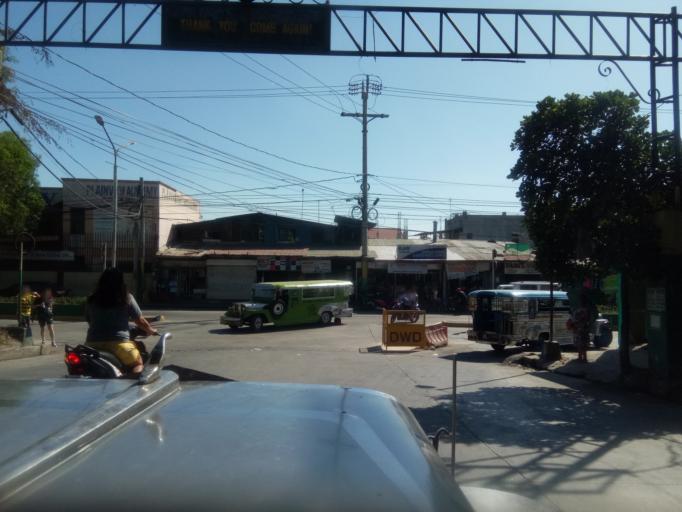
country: PH
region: Calabarzon
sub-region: Province of Cavite
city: Dasmarinas
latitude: 14.3096
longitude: 120.9688
